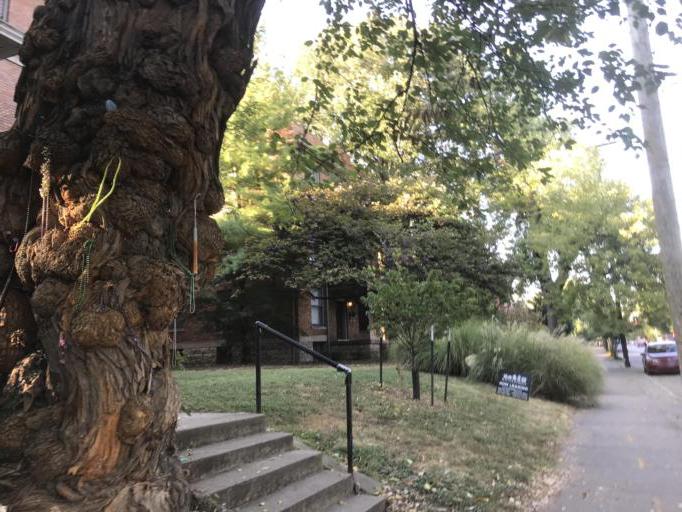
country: US
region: Kentucky
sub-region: Jefferson County
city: Louisville
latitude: 38.2319
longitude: -85.7644
